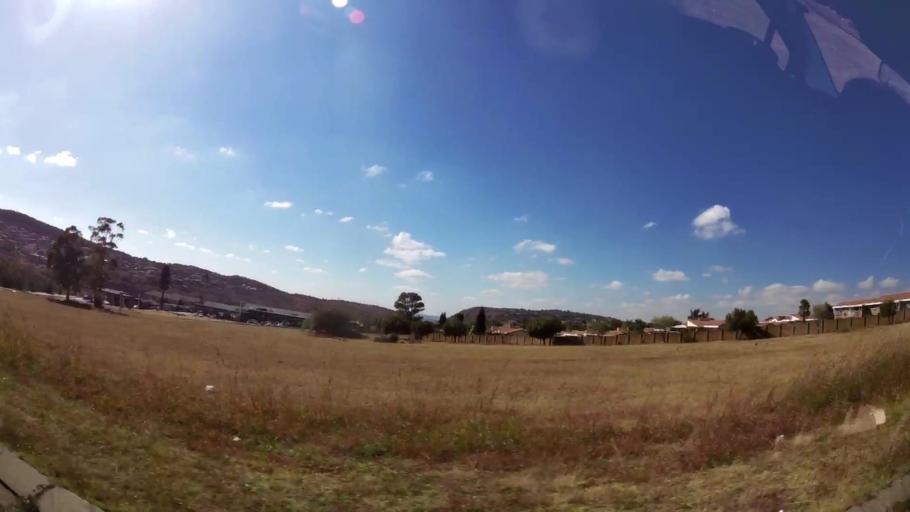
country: ZA
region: Gauteng
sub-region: West Rand District Municipality
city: Krugersdorp
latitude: -26.0942
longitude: 27.8250
